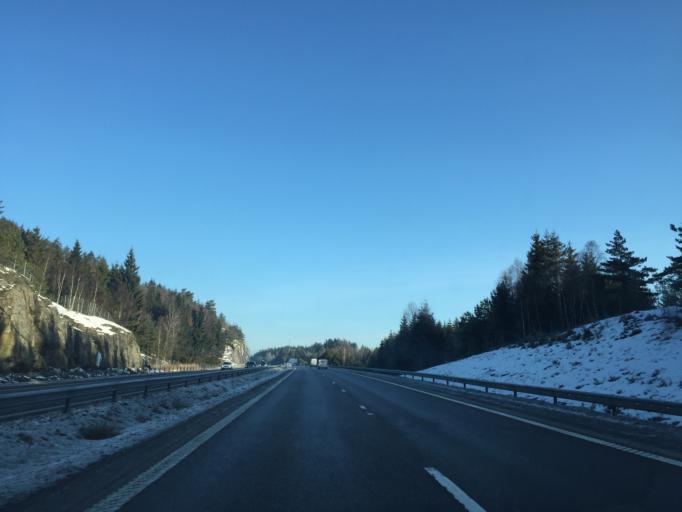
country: SE
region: Vaestra Goetaland
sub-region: Uddevalla Kommun
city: Ljungskile
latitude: 58.1748
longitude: 11.9019
